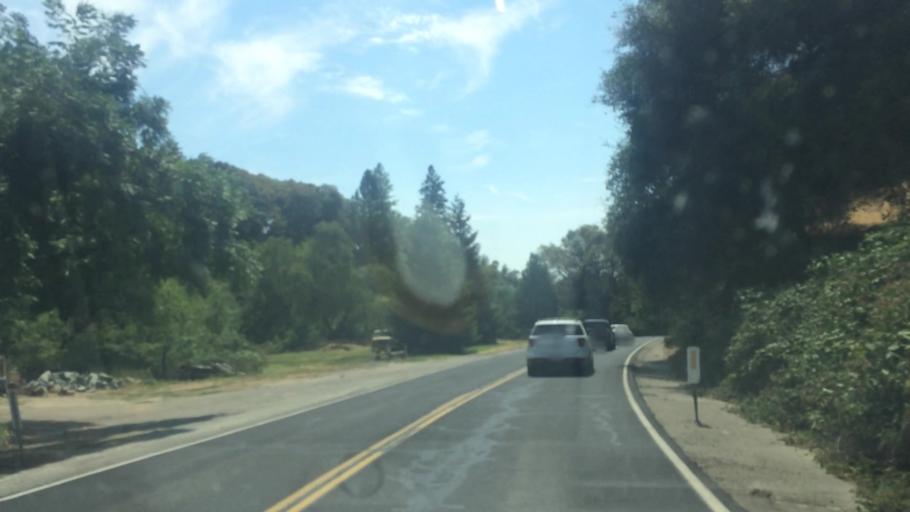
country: US
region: California
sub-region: Amador County
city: Pine Grove
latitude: 38.4126
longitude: -120.7018
